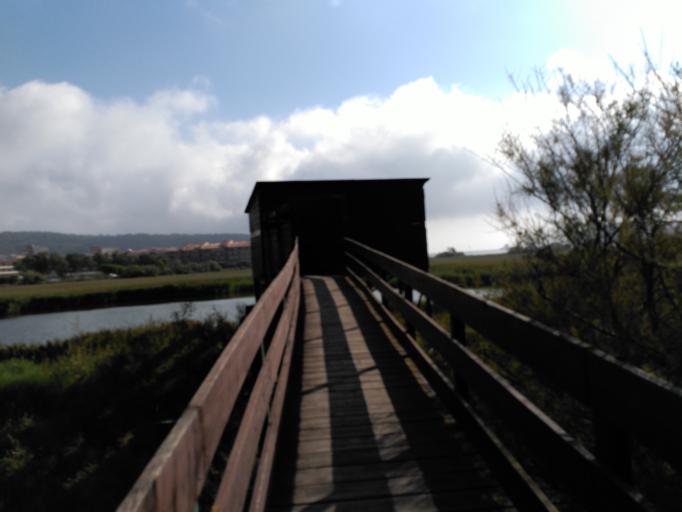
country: ES
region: Catalonia
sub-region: Provincia de Girona
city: Torroella de Montgri
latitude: 42.0457
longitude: 3.1926
